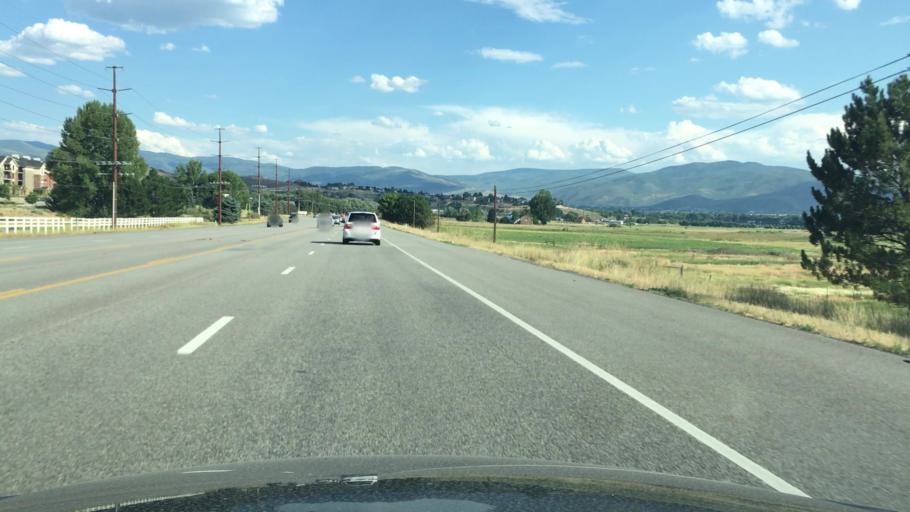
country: US
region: Utah
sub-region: Wasatch County
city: Heber
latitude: 40.5423
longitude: -111.4158
